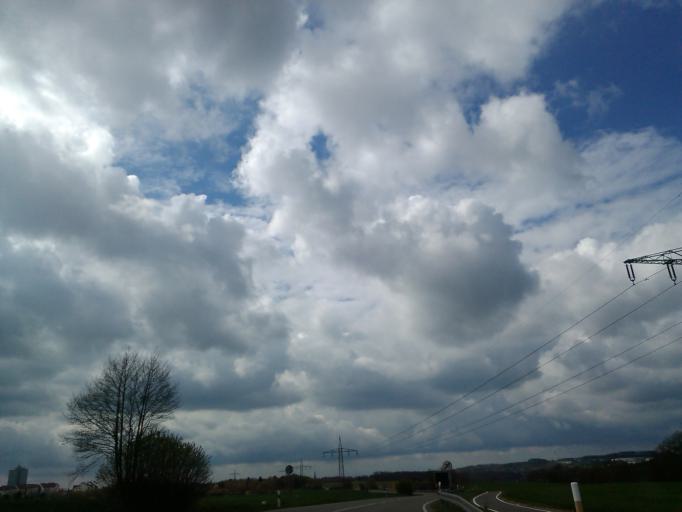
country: DE
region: Bavaria
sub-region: Swabia
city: Neu-Ulm
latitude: 48.4407
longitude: 10.0152
